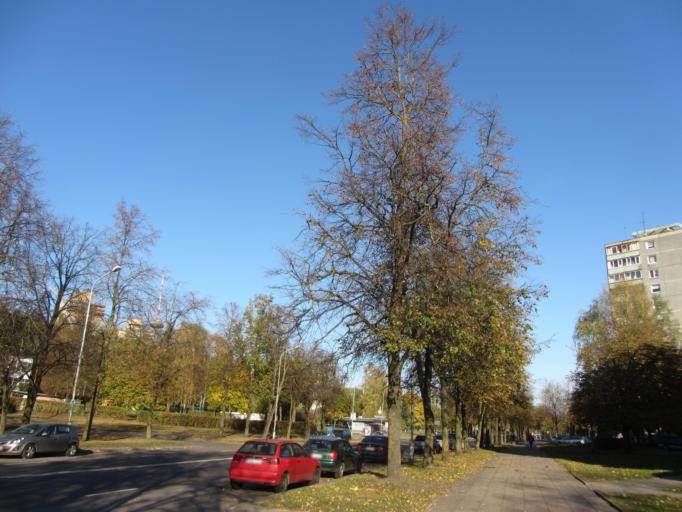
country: LT
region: Vilnius County
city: Lazdynai
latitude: 54.6758
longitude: 25.2056
